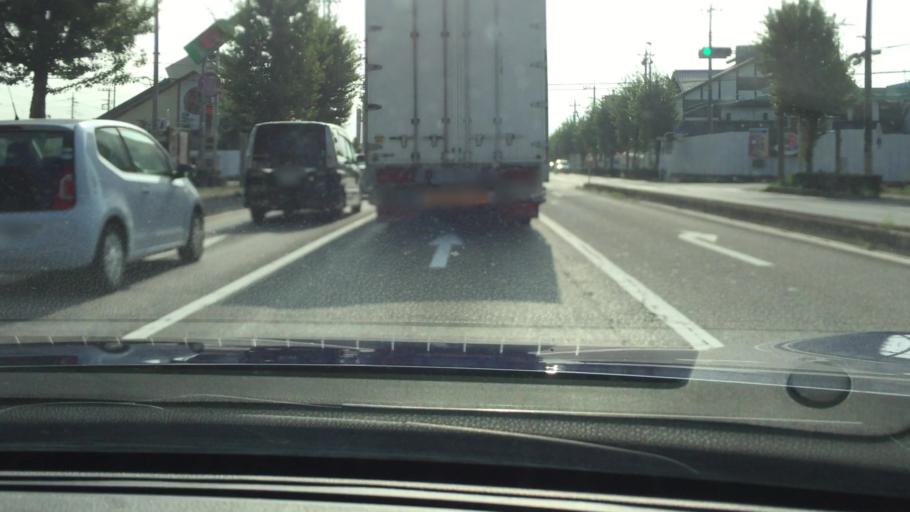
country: JP
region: Gunma
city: Tatebayashi
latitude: 36.2450
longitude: 139.4591
